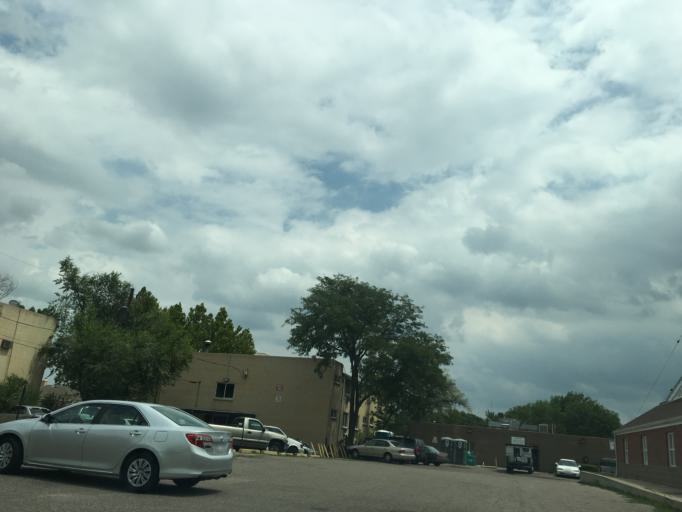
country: US
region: Colorado
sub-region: Arapahoe County
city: Sheridan
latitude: 39.6828
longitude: -105.0263
